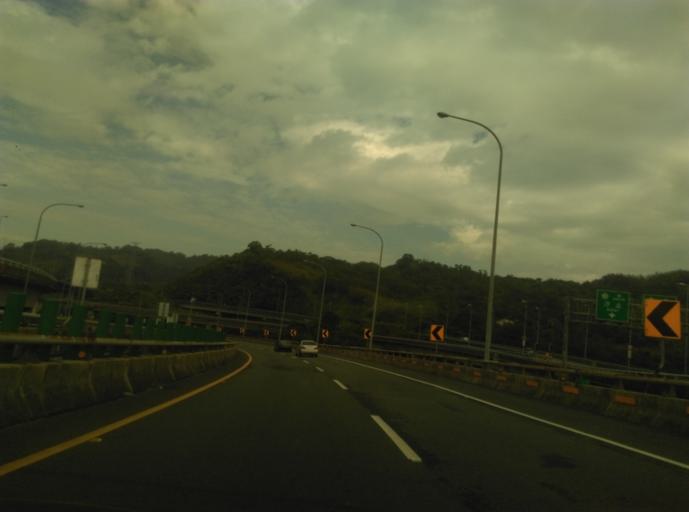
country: TW
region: Taiwan
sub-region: Keelung
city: Keelung
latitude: 25.1238
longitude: 121.6986
